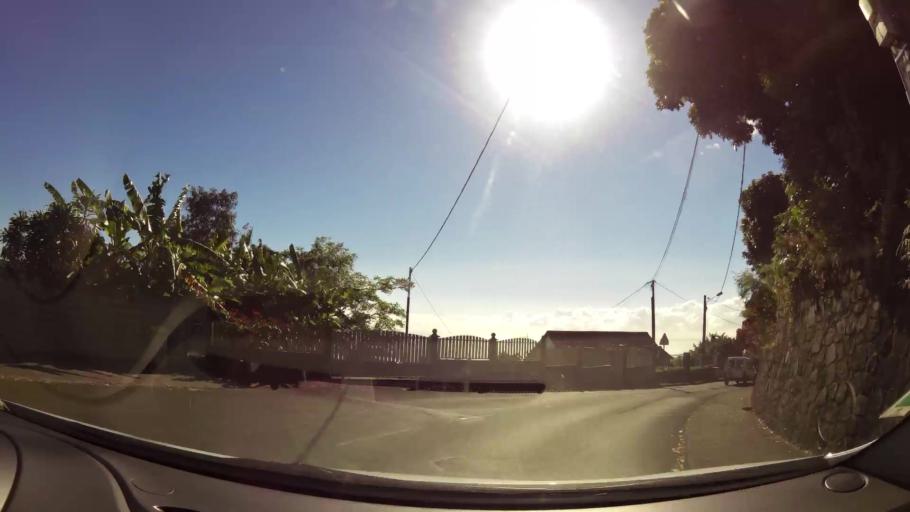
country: RE
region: Reunion
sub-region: Reunion
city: Saint-Denis
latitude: -20.9165
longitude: 55.4761
